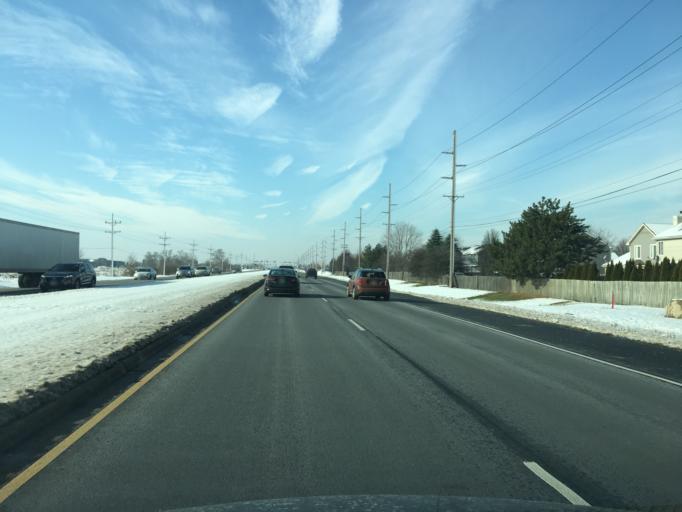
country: US
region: Illinois
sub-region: DuPage County
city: Naperville
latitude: 41.7474
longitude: -88.1909
